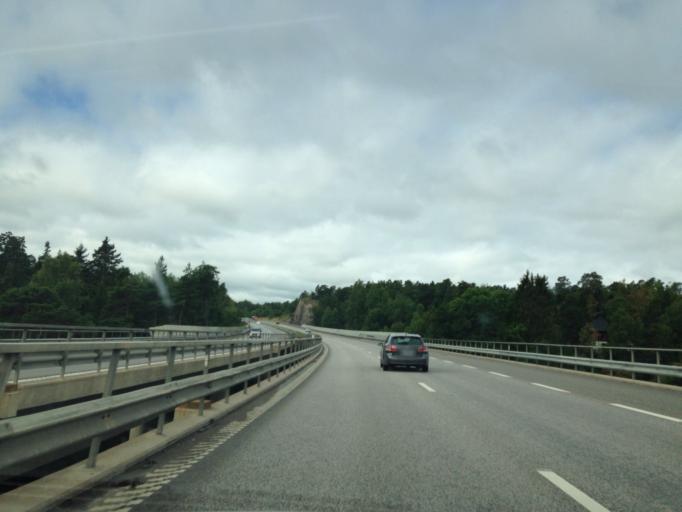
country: SE
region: Stockholm
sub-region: Nacka Kommun
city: Boo
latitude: 59.3291
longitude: 18.3124
